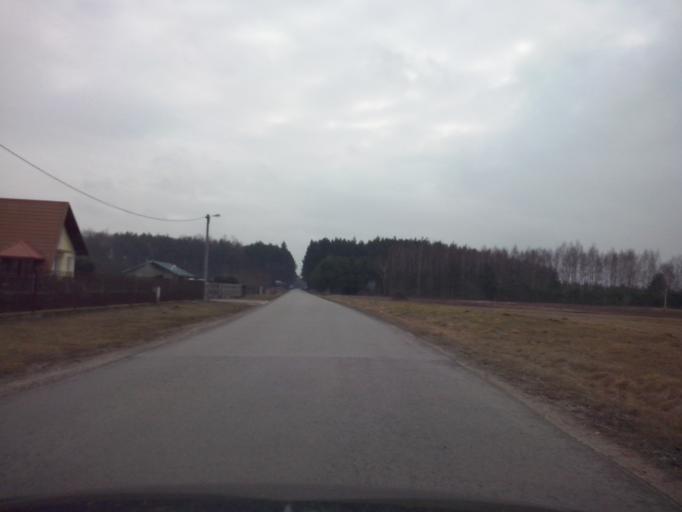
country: PL
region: Subcarpathian Voivodeship
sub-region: Powiat nizanski
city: Bieliny
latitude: 50.4612
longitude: 22.2822
